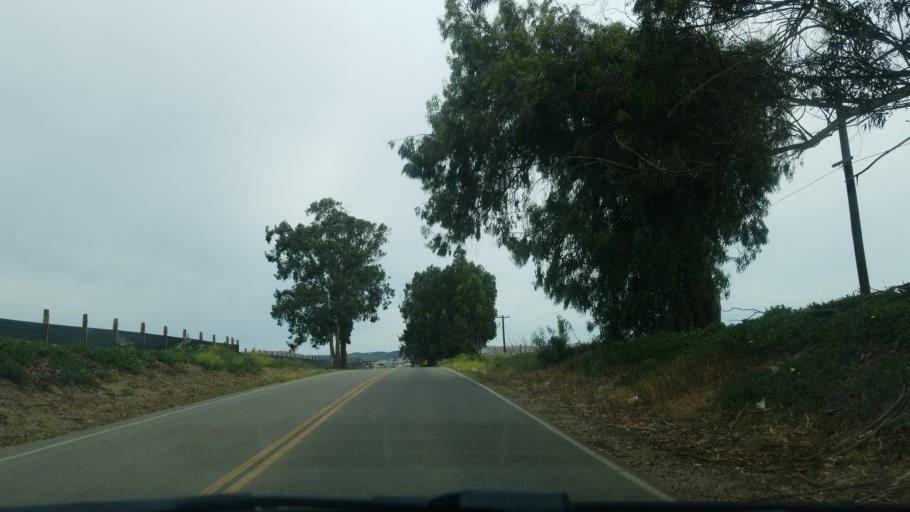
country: US
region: California
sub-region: Santa Barbara County
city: Santa Maria
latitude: 34.9135
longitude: -120.4903
